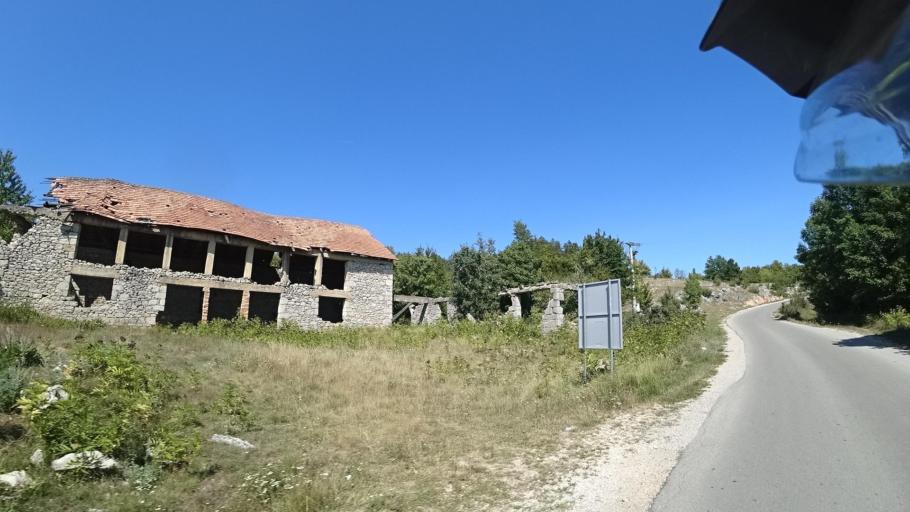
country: HR
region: Licko-Senjska
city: Popovaca
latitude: 44.7291
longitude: 15.2887
